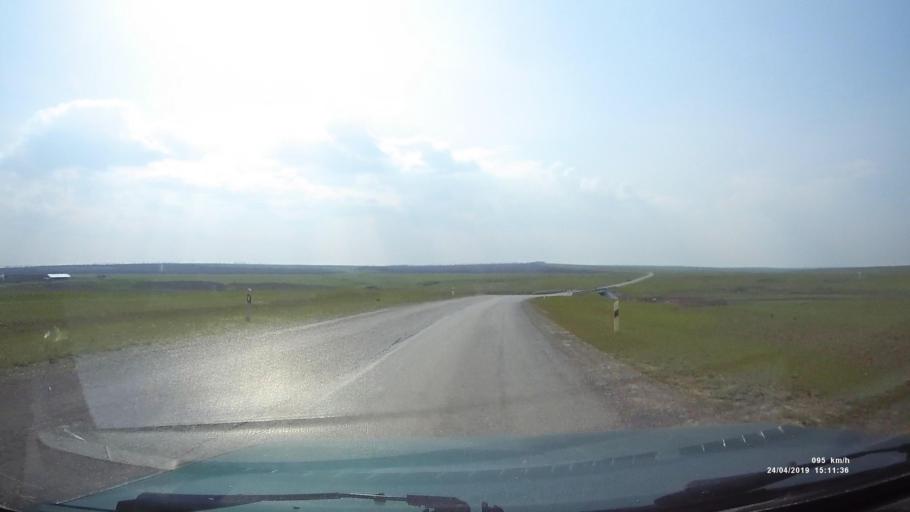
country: RU
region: Rostov
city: Remontnoye
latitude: 46.5440
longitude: 43.3181
